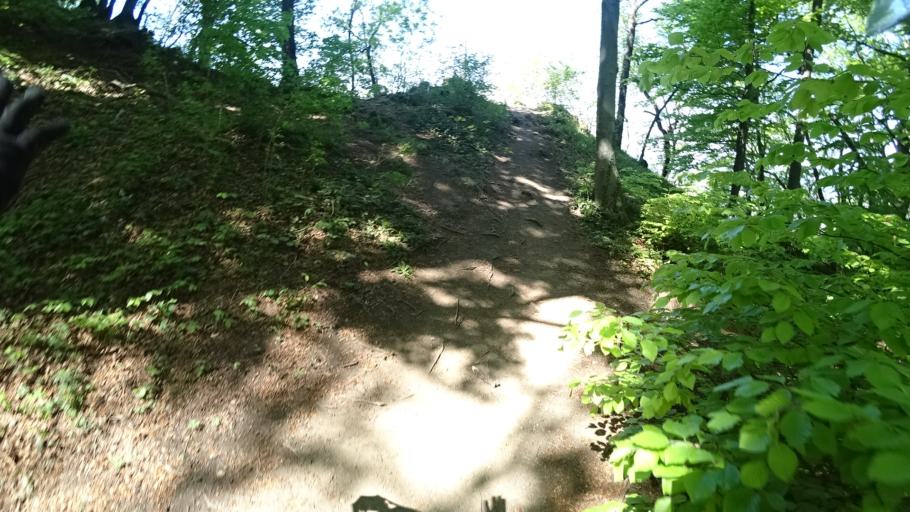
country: HR
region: Zagrebacka
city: Jablanovec
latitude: 45.8695
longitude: 15.8547
